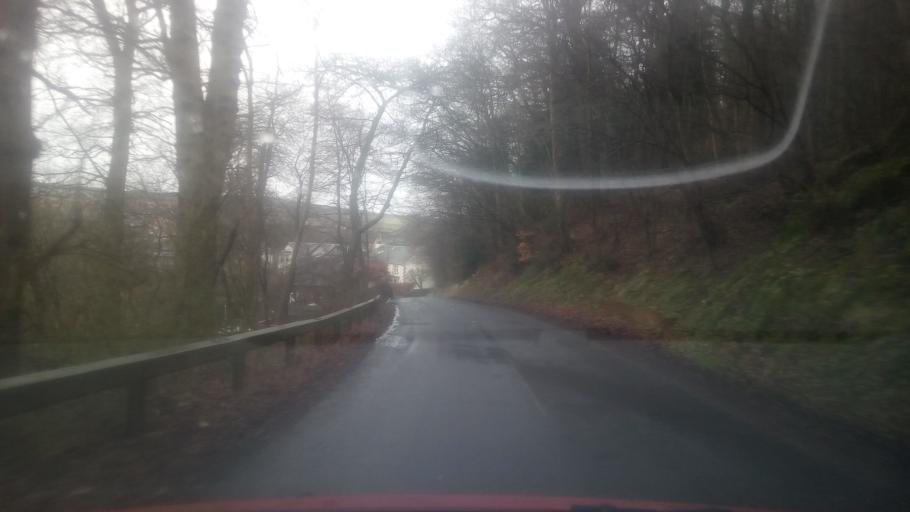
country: GB
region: Scotland
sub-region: The Scottish Borders
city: Earlston
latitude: 55.6339
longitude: -2.6760
